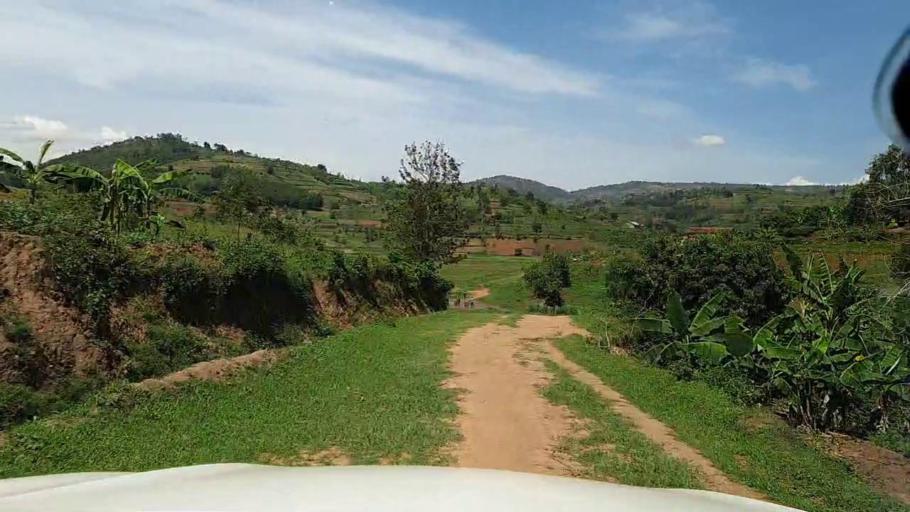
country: RW
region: Southern Province
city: Butare
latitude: -2.7295
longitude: 29.8084
